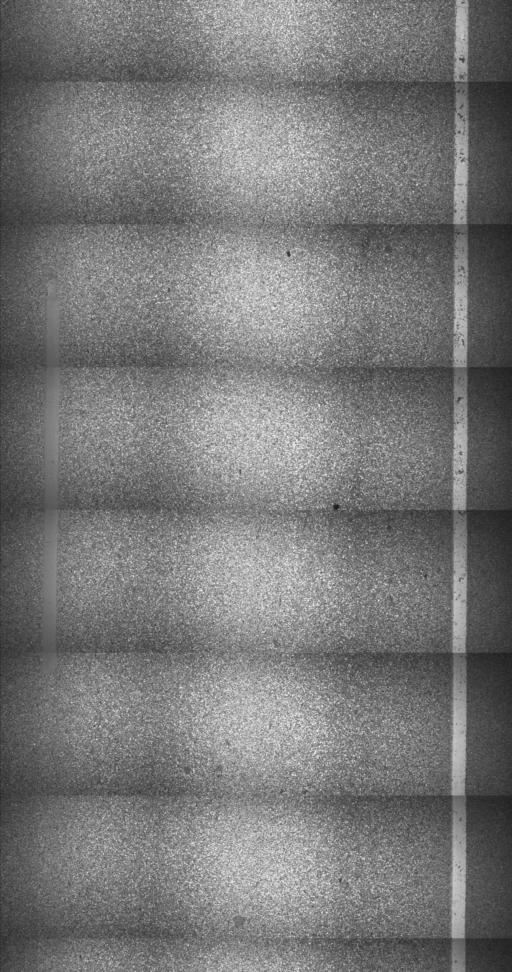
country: US
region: Vermont
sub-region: Chittenden County
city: Jericho
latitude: 44.6418
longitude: -72.9410
